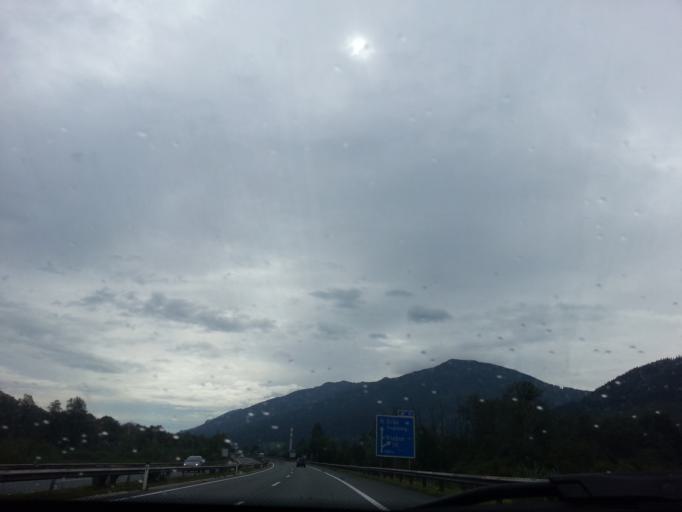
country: AT
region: Styria
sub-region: Politischer Bezirk Liezen
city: Trieben
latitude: 47.4992
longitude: 14.4643
